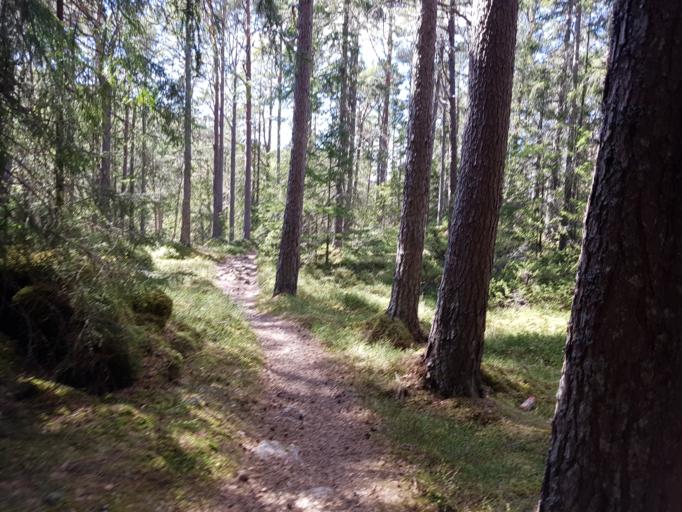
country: NO
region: Sor-Trondelag
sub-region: Trondheim
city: Trondheim
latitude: 63.4435
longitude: 10.3089
